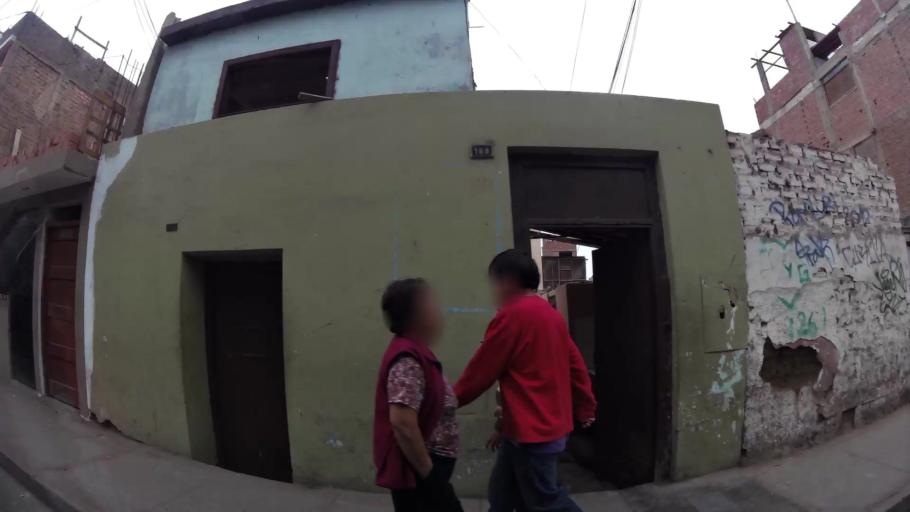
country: PE
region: Lima
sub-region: Lima
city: Surco
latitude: -12.1479
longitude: -77.0153
